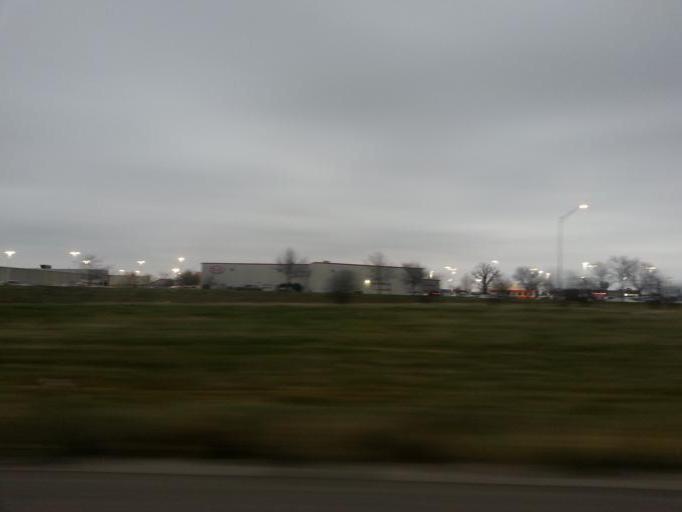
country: US
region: Iowa
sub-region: Linn County
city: Hiawatha
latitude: 42.0461
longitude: -91.6858
